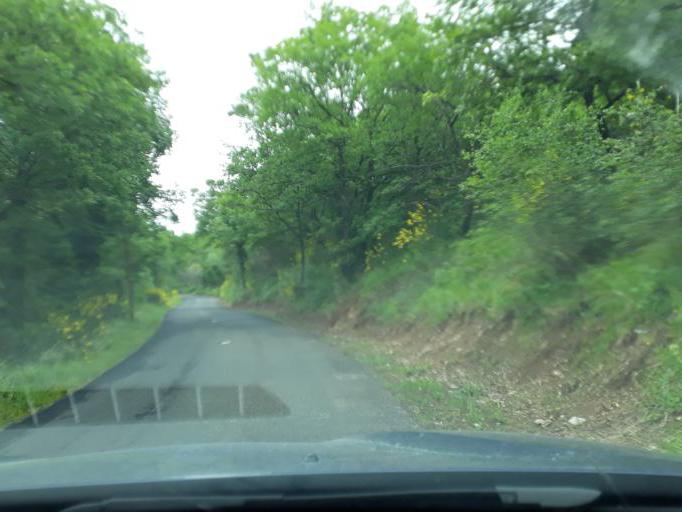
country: FR
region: Languedoc-Roussillon
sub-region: Departement de l'Herault
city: Lodeve
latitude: 43.7737
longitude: 3.2965
